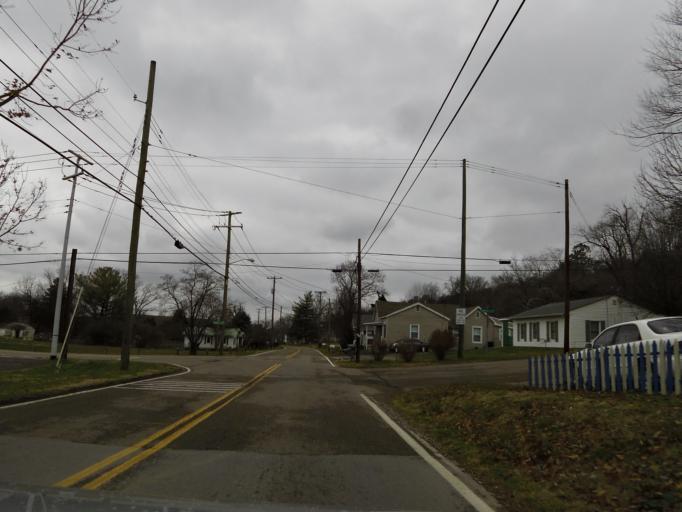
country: US
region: Tennessee
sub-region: Knox County
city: Knoxville
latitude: 35.9658
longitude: -83.9662
